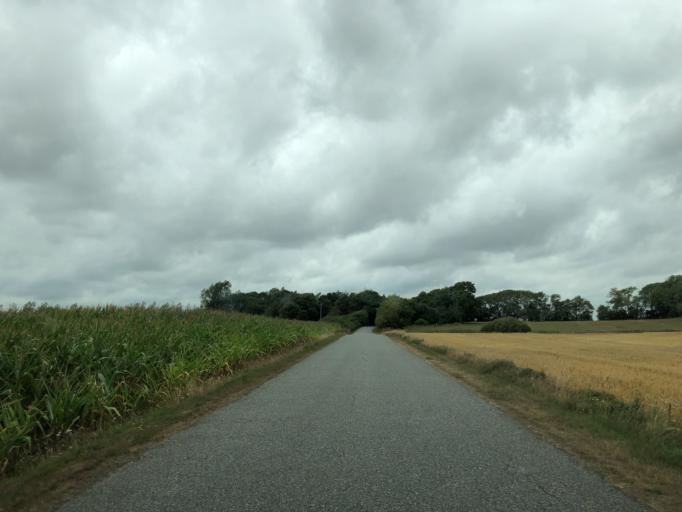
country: DK
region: Central Jutland
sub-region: Ringkobing-Skjern Kommune
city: Videbaek
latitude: 56.0993
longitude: 8.4892
